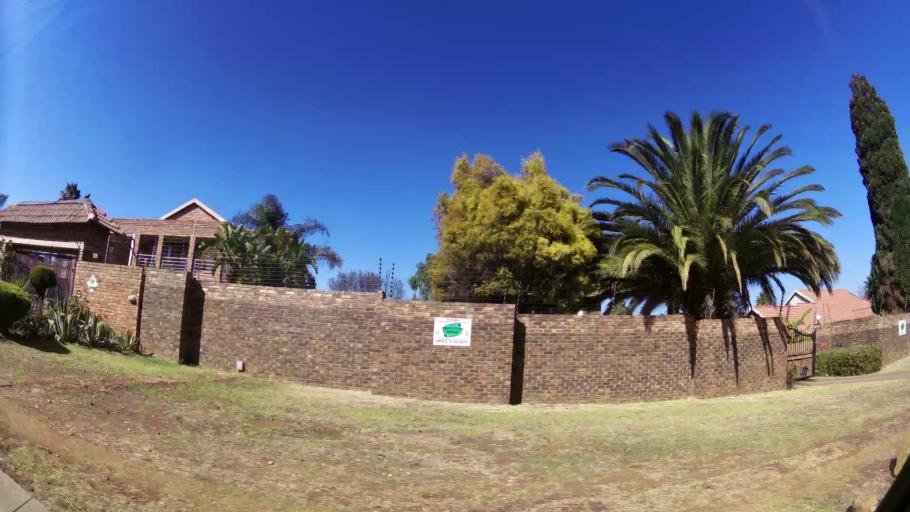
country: ZA
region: Gauteng
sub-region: Ekurhuleni Metropolitan Municipality
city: Germiston
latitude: -26.2996
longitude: 28.0952
